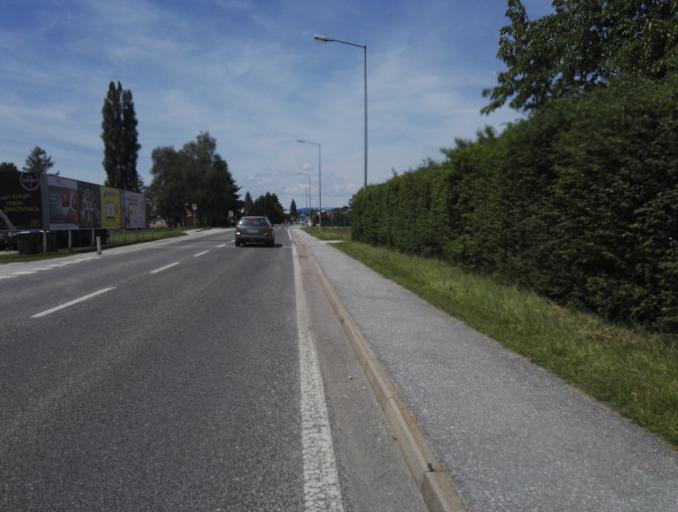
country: AT
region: Styria
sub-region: Politischer Bezirk Graz-Umgebung
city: Gossendorf
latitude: 46.9852
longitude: 15.4605
